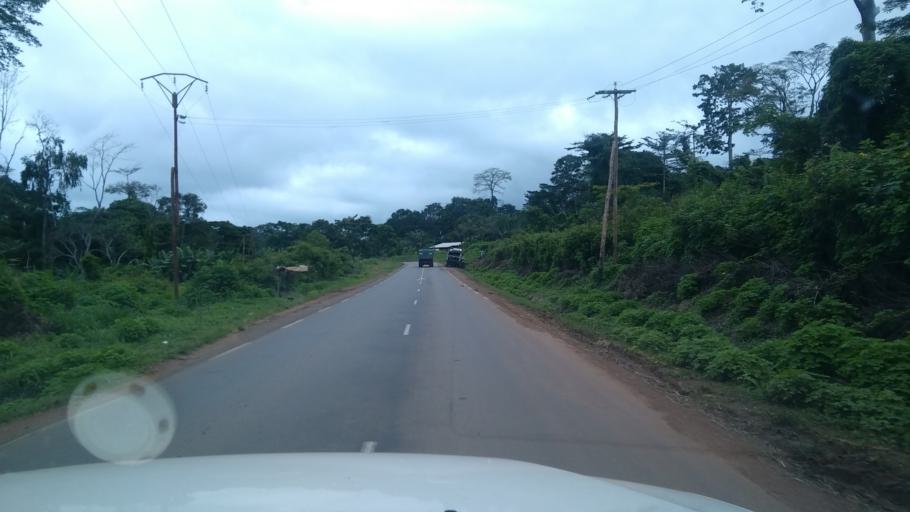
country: CM
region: Centre
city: Mbalmayo
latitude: 3.5931
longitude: 11.5165
